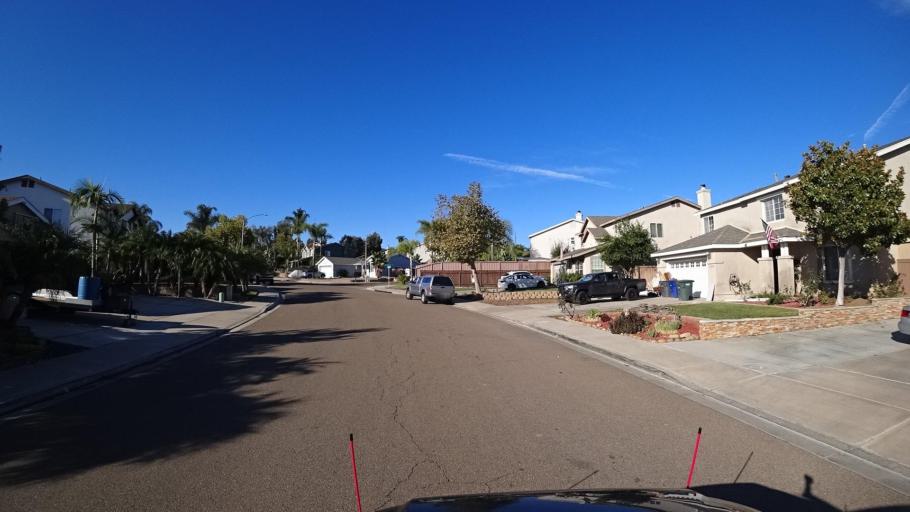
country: US
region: California
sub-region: San Diego County
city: Lakeside
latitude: 32.8495
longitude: -116.9079
